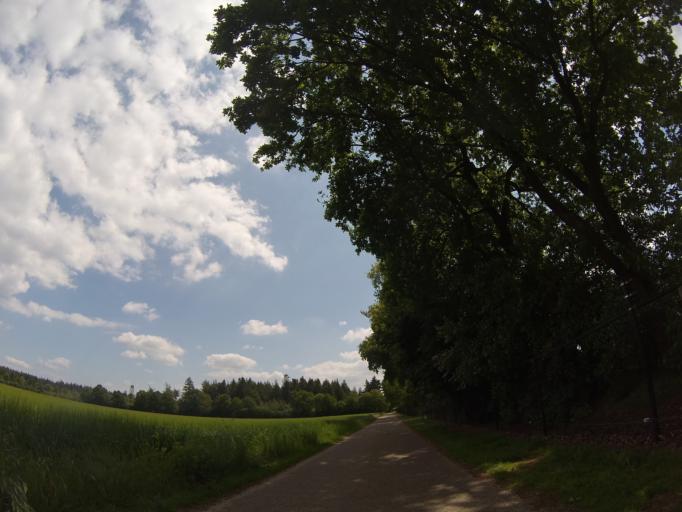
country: NL
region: Gelderland
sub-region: Gemeente Barneveld
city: Garderen
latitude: 52.2328
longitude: 5.6660
